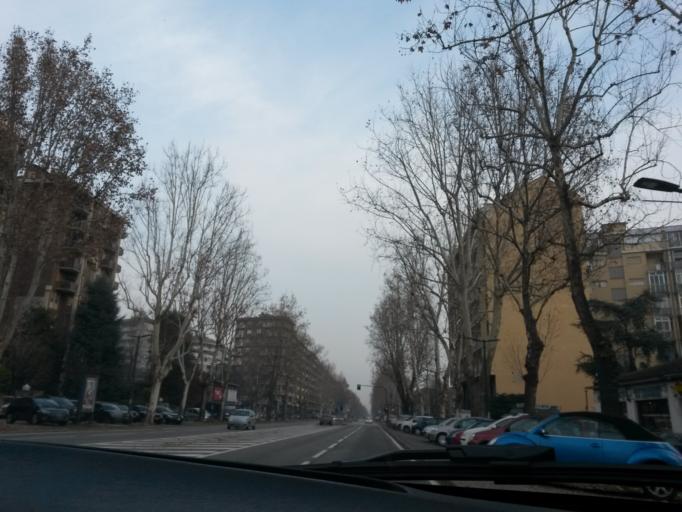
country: IT
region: Piedmont
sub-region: Provincia di Torino
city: Lesna
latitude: 45.0746
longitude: 7.6222
